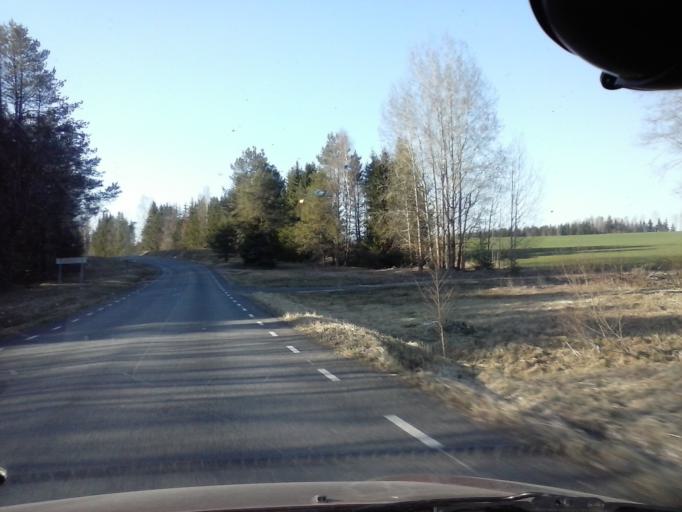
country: EE
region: Tartu
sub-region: UElenurme vald
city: Ulenurme
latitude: 58.1749
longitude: 26.8327
